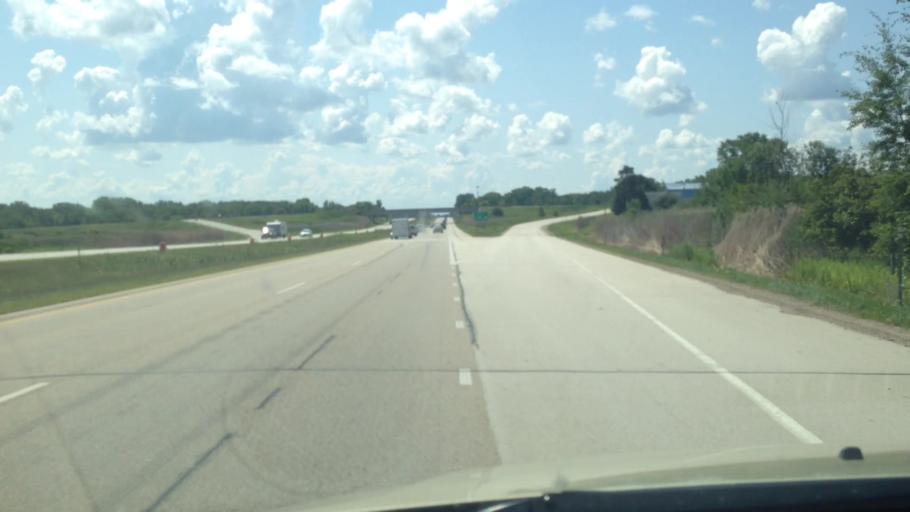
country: US
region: Wisconsin
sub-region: Brown County
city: Suamico
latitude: 44.6821
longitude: -88.0511
